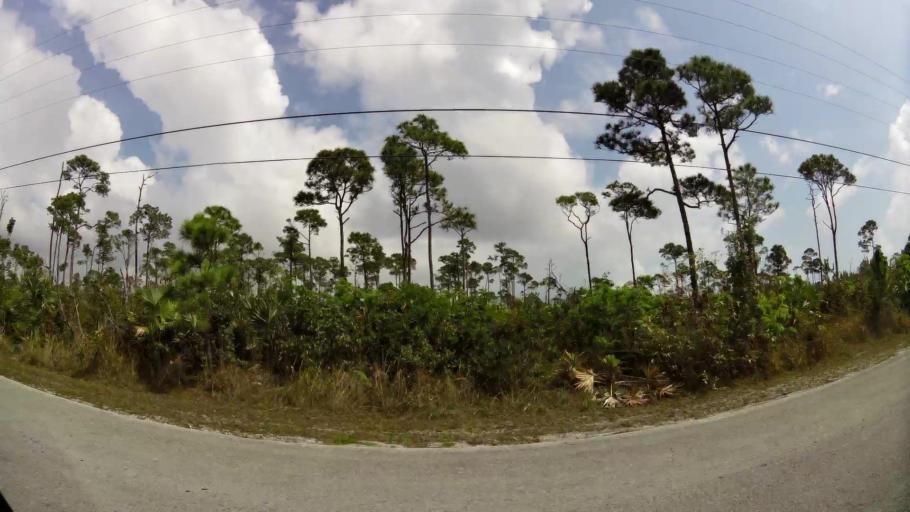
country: BS
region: Freeport
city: Lucaya
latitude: 26.5275
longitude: -78.6254
